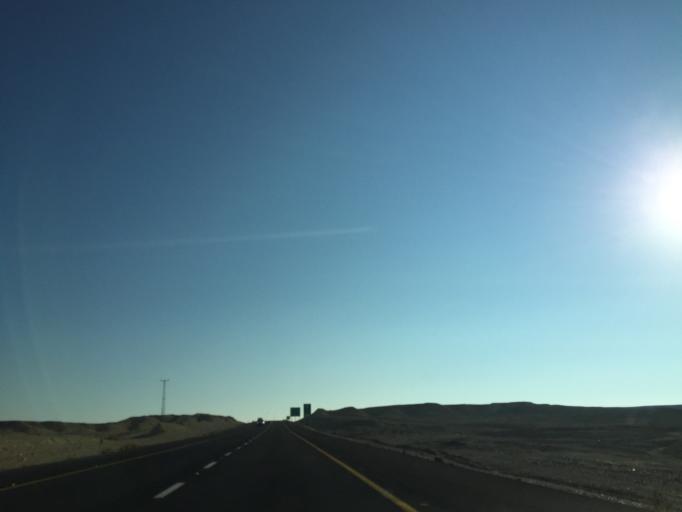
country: IL
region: Southern District
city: Mitzpe Ramon
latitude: 30.2779
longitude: 35.0136
